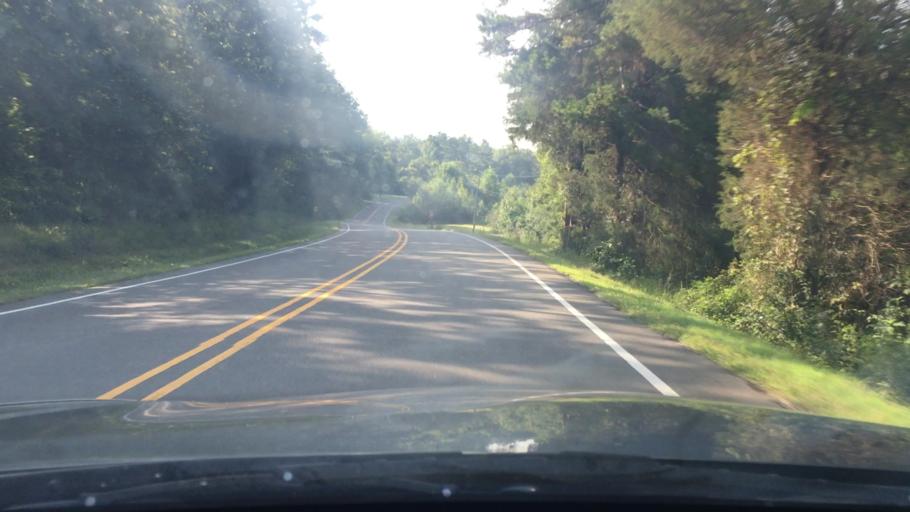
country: US
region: North Carolina
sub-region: Alamance County
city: Green Level
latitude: 36.2554
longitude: -79.3340
